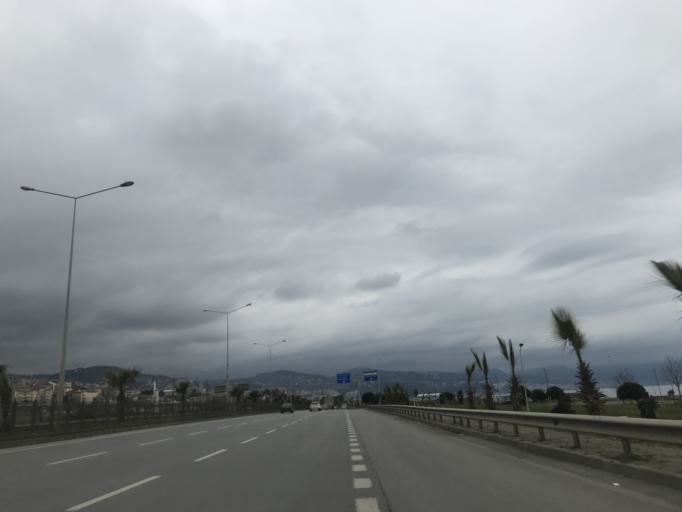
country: TR
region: Trabzon
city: Trabzon
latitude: 41.0116
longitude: 39.7163
